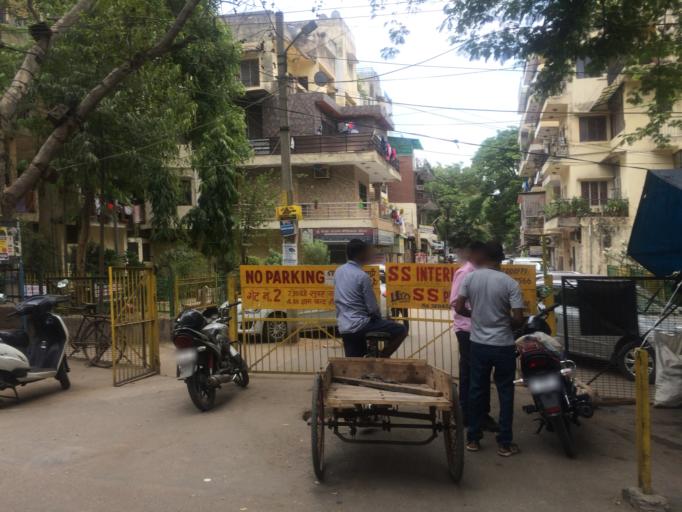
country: IN
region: NCT
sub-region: New Delhi
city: New Delhi
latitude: 28.5346
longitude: 77.2308
